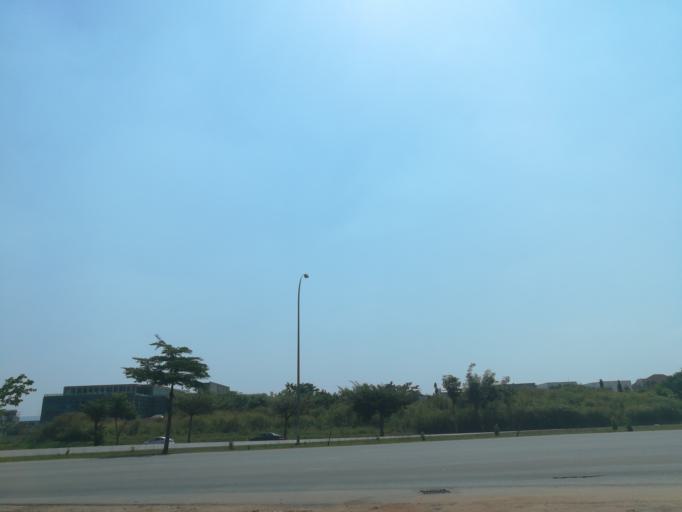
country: NG
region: Abuja Federal Capital Territory
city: Abuja
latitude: 9.0775
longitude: 7.4336
